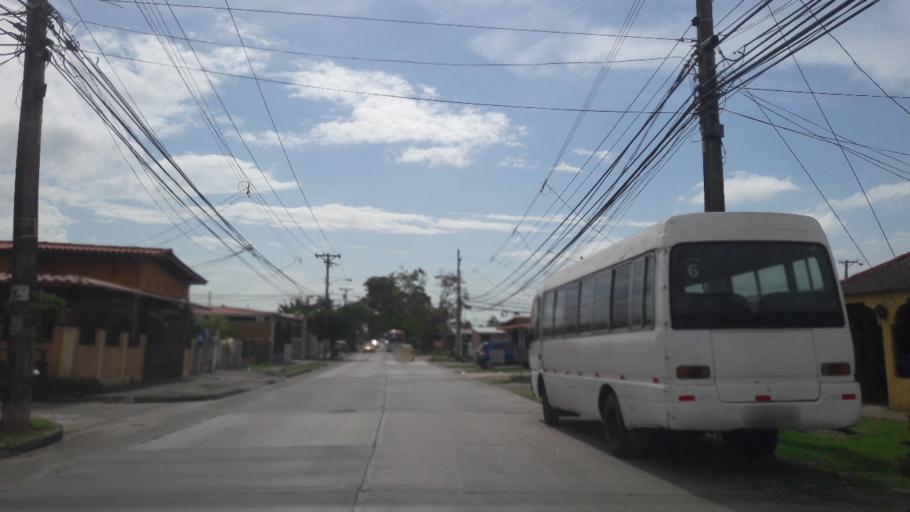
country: PA
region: Panama
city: Tocumen
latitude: 9.0576
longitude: -79.4186
